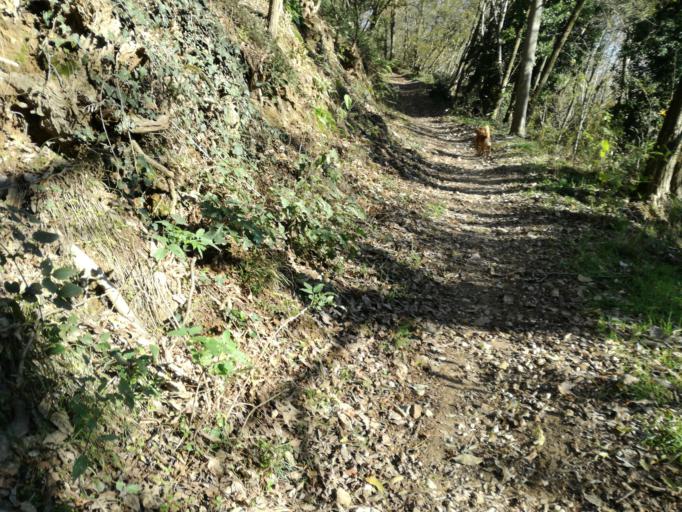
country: IT
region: Veneto
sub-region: Provincia di Padova
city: Arqua Petrarca
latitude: 45.2789
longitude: 11.7353
